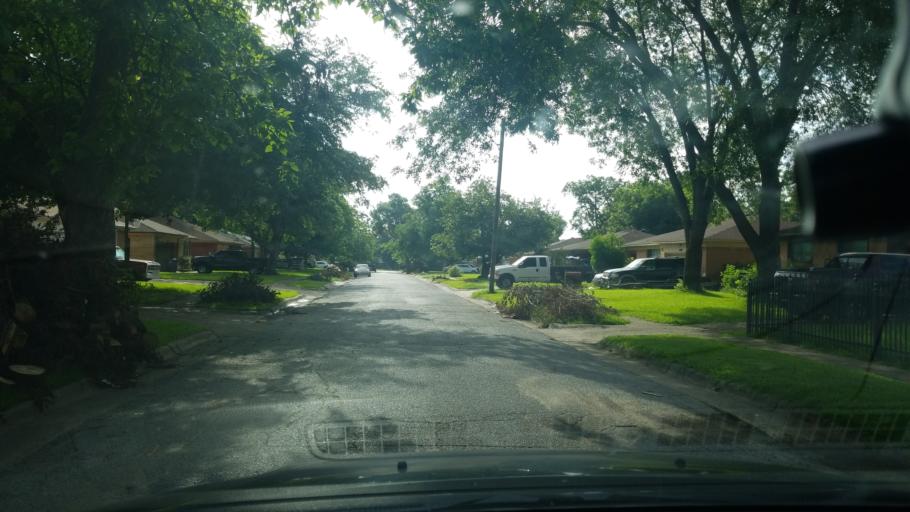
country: US
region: Texas
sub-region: Dallas County
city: Balch Springs
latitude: 32.7469
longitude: -96.6649
